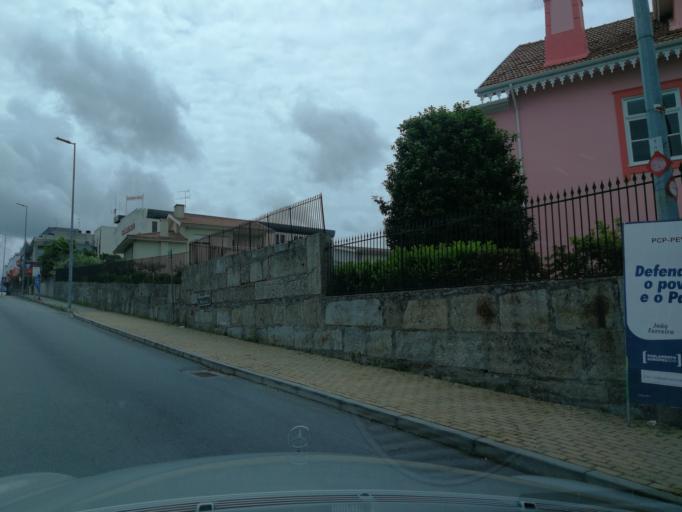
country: PT
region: Braga
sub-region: Amares
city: Amares
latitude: 41.6277
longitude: -8.3701
